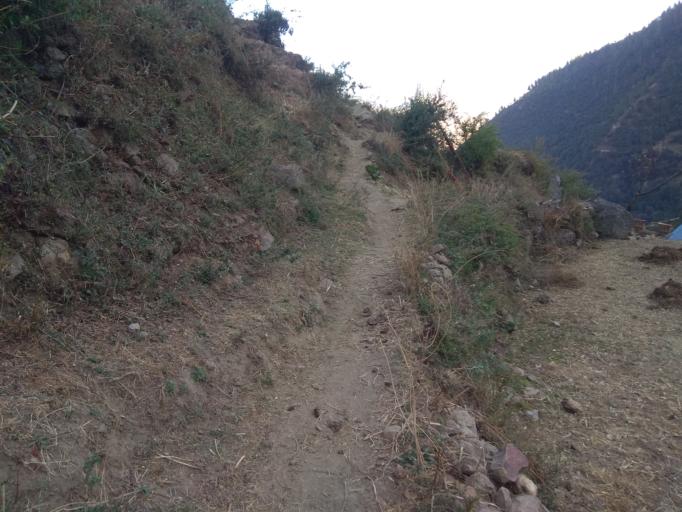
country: NP
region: Mid Western
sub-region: Karnali Zone
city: Jumla
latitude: 29.3238
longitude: 81.7220
